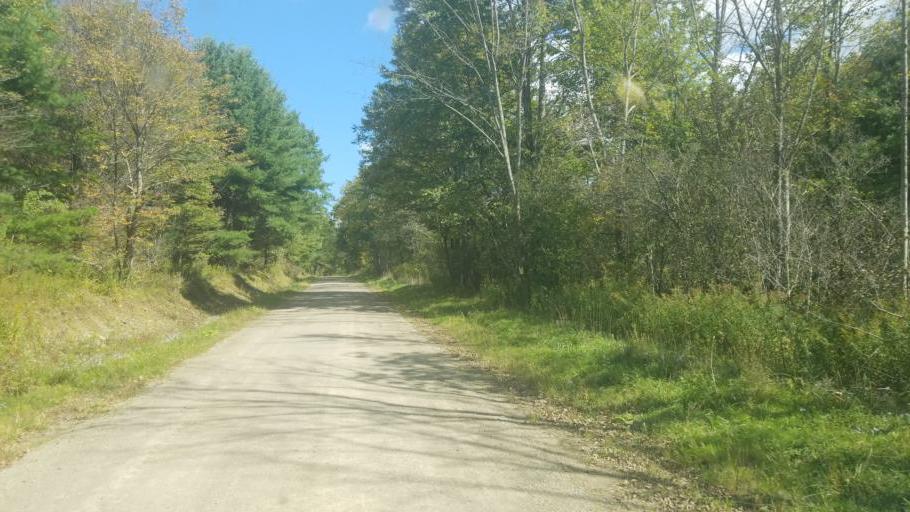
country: US
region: New York
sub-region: Allegany County
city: Cuba
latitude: 42.1865
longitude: -78.3305
